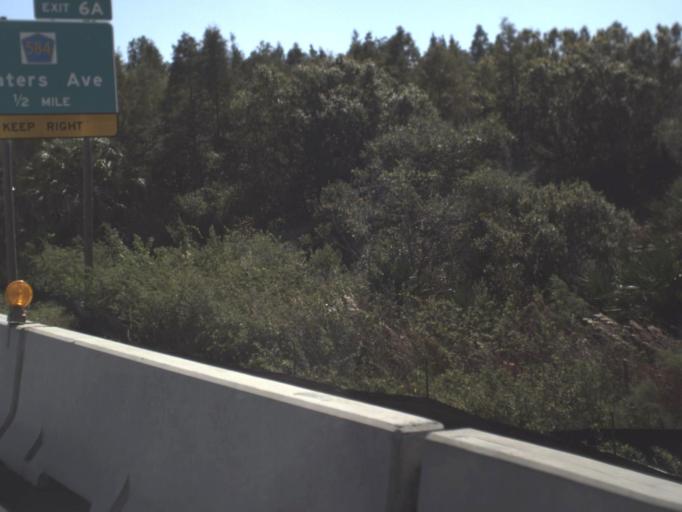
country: US
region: Florida
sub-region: Hillsborough County
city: Town 'n' Country
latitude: 28.0355
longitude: -82.5474
